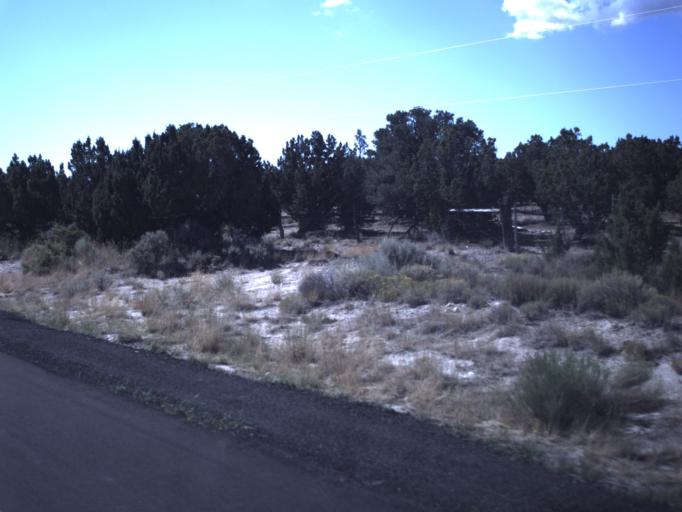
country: US
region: Utah
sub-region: Utah County
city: Eagle Mountain
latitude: 40.0366
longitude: -112.2875
